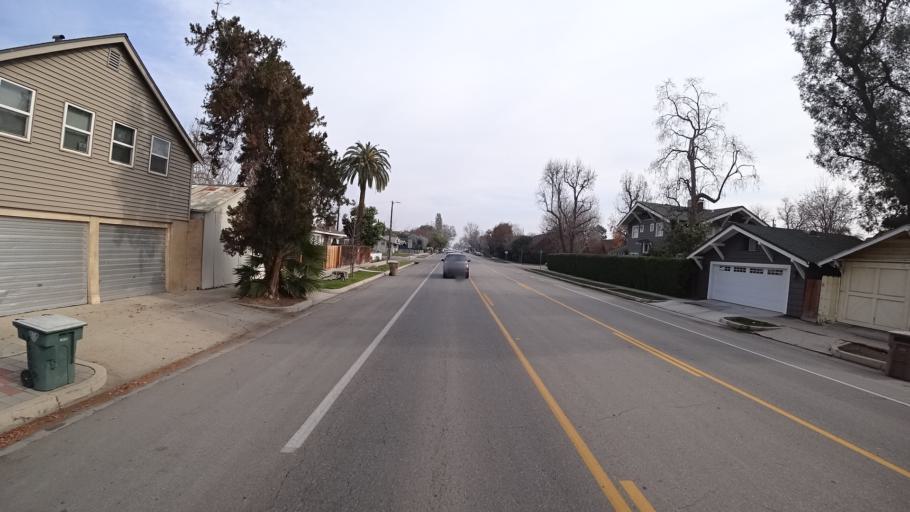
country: US
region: California
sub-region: Kern County
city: Bakersfield
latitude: 35.3782
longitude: -119.0277
